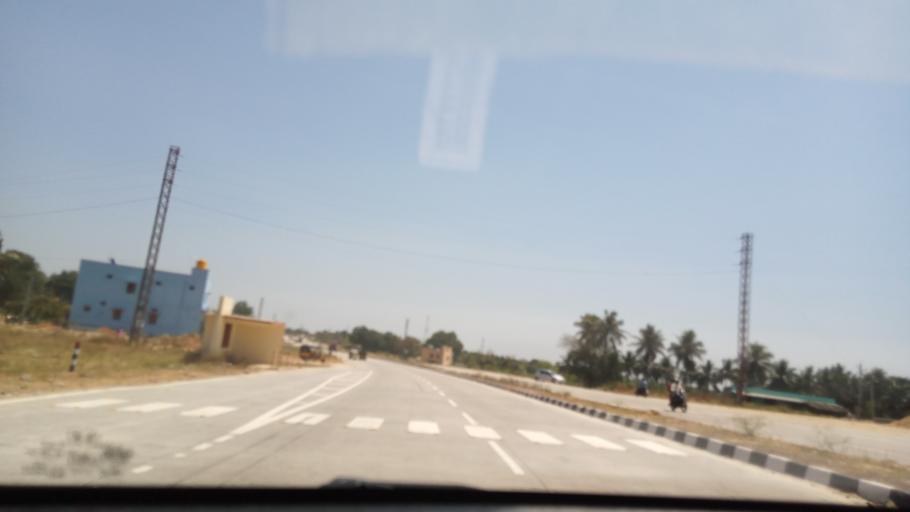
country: IN
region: Andhra Pradesh
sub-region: Chittoor
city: Chittoor
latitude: 13.1961
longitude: 78.9895
